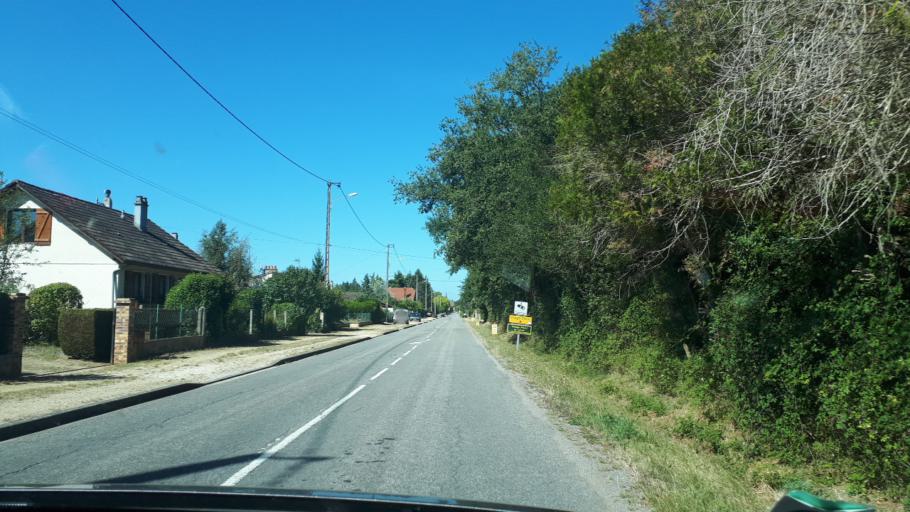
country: FR
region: Centre
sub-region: Departement du Loiret
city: Cerdon
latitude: 47.6372
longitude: 2.3769
